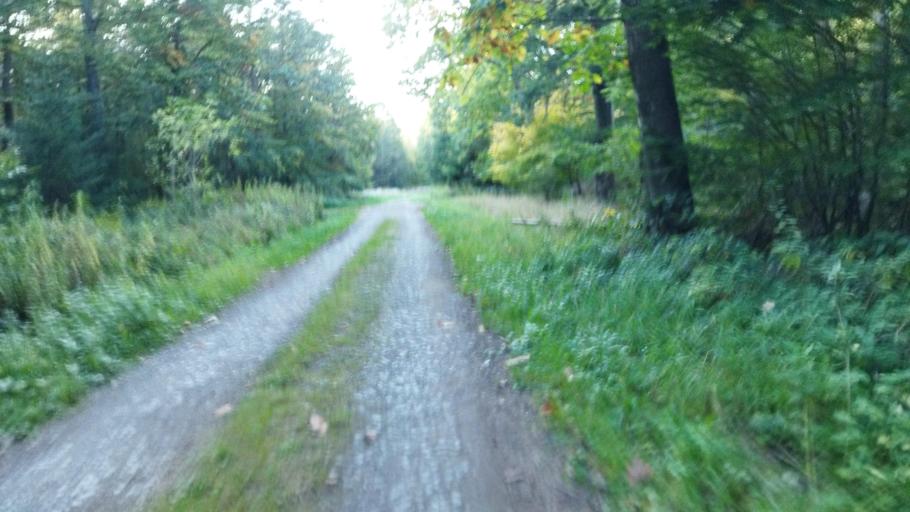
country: DE
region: Baden-Wuerttemberg
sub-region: Regierungsbezirk Stuttgart
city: Freudental
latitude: 49.0143
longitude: 9.0296
